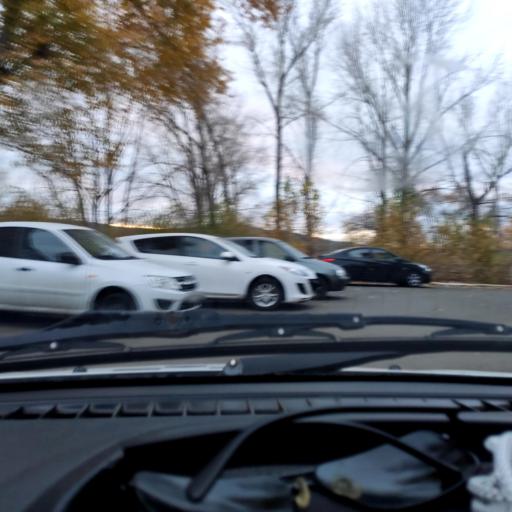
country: RU
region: Samara
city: Zhigulevsk
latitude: 53.4622
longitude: 49.5390
